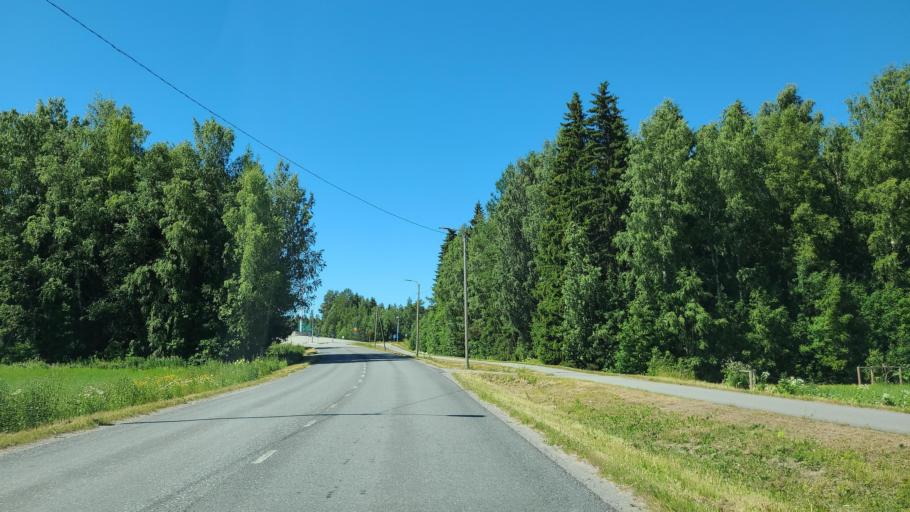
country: FI
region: Ostrobothnia
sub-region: Vaasa
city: Ristinummi
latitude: 63.0550
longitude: 21.7231
